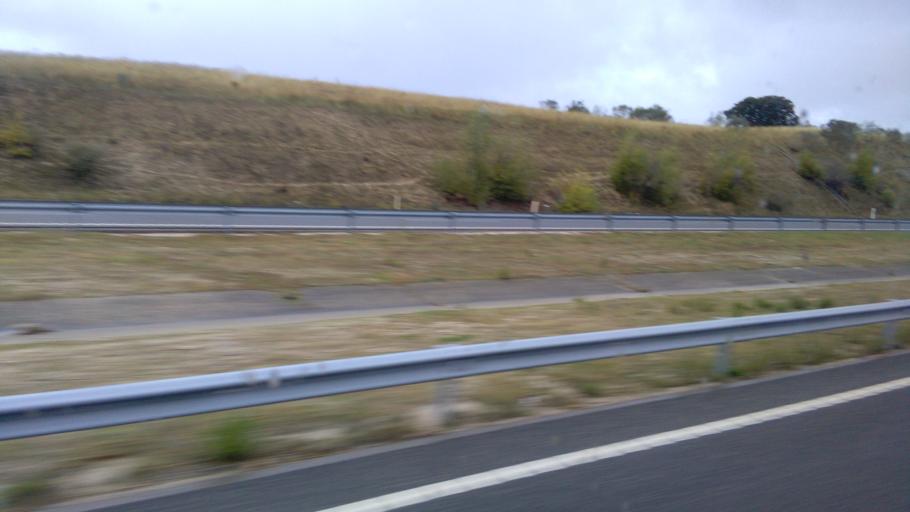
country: ES
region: Madrid
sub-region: Provincia de Madrid
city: Arroyomolinos
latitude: 40.2571
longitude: -3.9303
